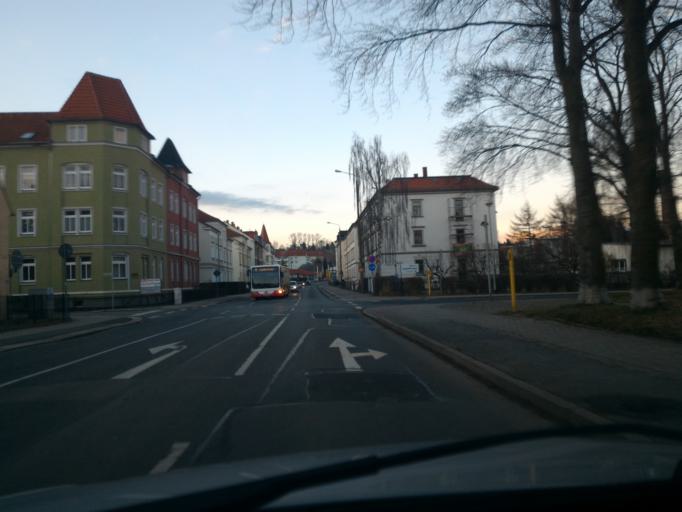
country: DE
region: Saxony
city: Zittau
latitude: 50.8962
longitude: 14.7925
